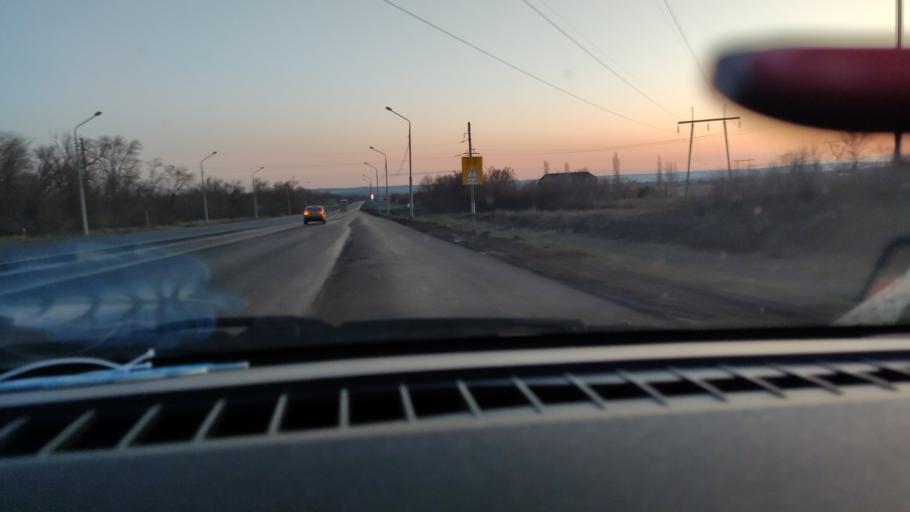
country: RU
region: Saratov
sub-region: Saratovskiy Rayon
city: Saratov
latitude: 51.6731
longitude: 46.0007
